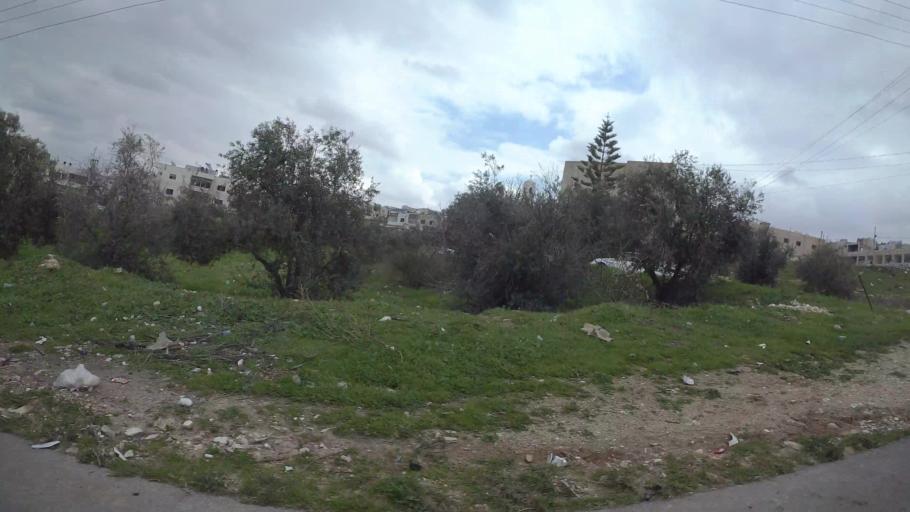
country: JO
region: Amman
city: Al Jubayhah
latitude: 32.0368
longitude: 35.8306
